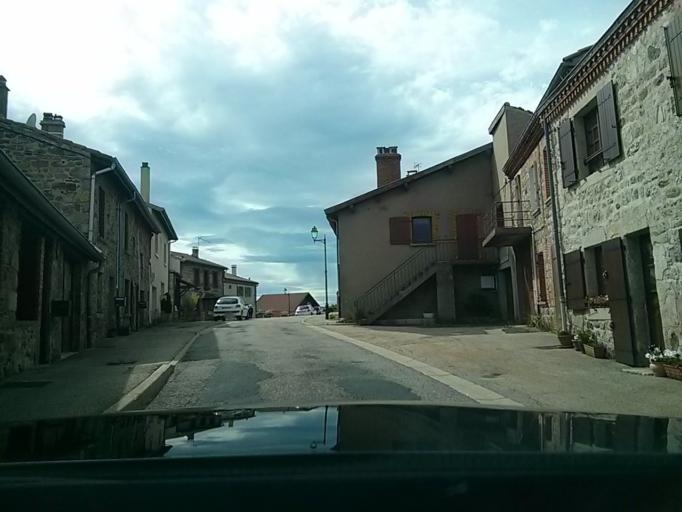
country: FR
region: Rhone-Alpes
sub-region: Departement de la Loire
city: Bourg-Argental
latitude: 45.3690
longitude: 4.5154
